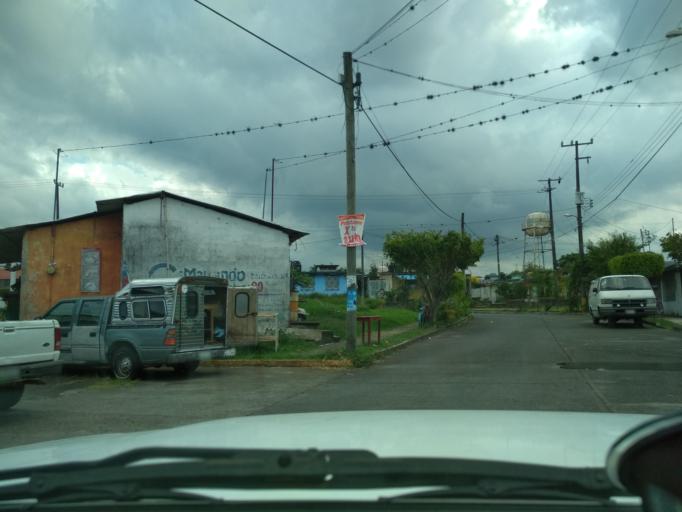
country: MX
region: Veracruz
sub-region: Cordoba
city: San Jose de Abajo [Unidad Habitacional]
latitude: 18.9205
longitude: -96.9633
